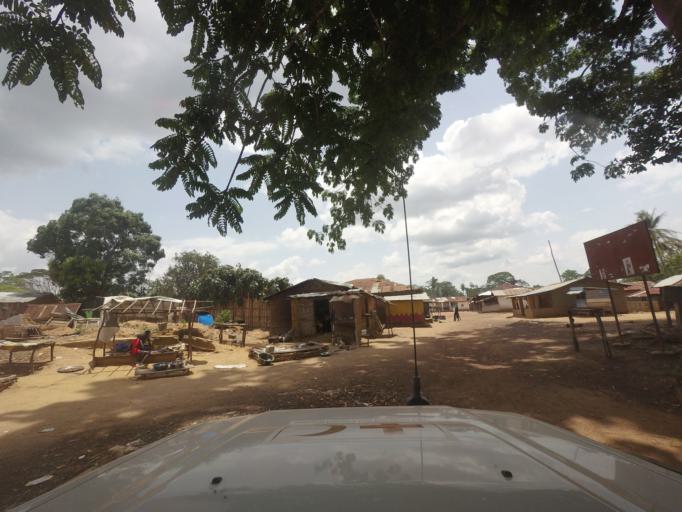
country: LR
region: Bong
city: Gbarnga
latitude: 7.1282
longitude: -9.2277
